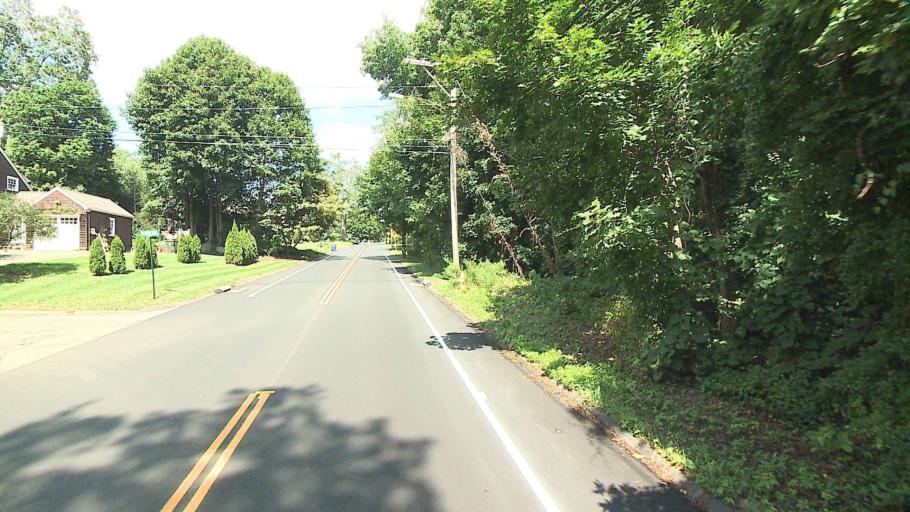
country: US
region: Connecticut
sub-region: Fairfield County
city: Trumbull
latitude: 41.2347
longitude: -73.1619
